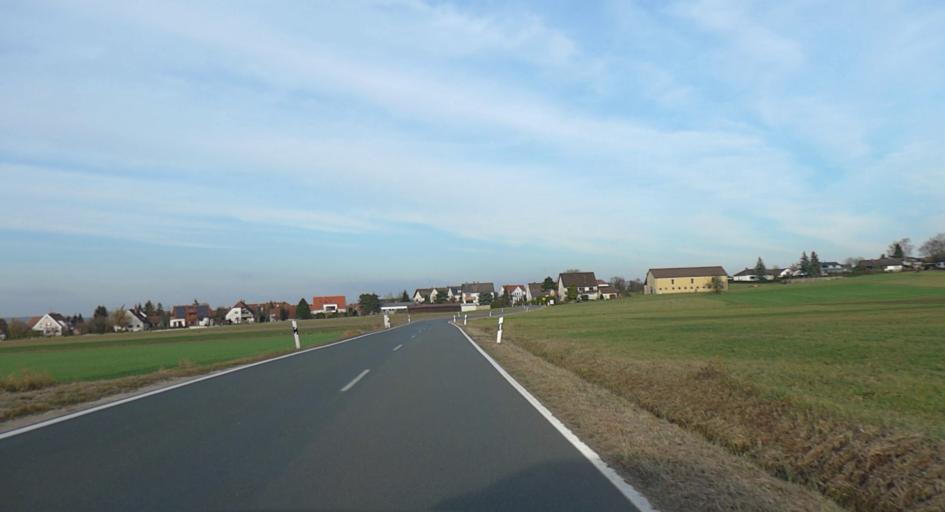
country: DE
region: Bavaria
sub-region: Regierungsbezirk Mittelfranken
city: Baiersdorf
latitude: 49.6414
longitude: 11.0382
